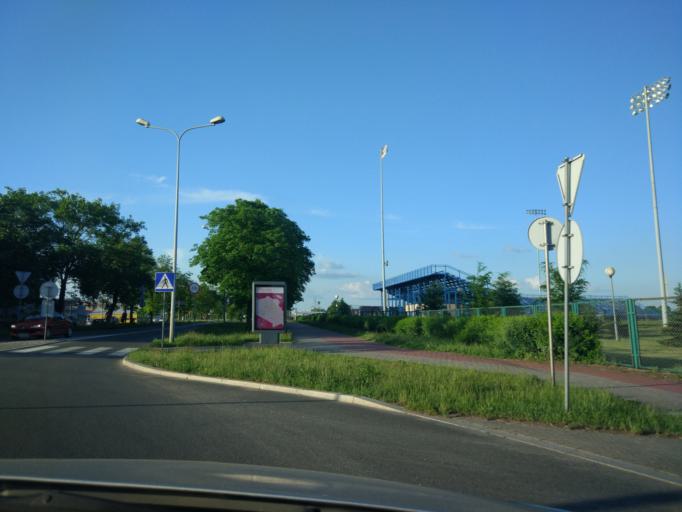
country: PL
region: Lodz Voivodeship
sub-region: Powiat kutnowski
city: Kutno
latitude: 52.2426
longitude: 19.3746
